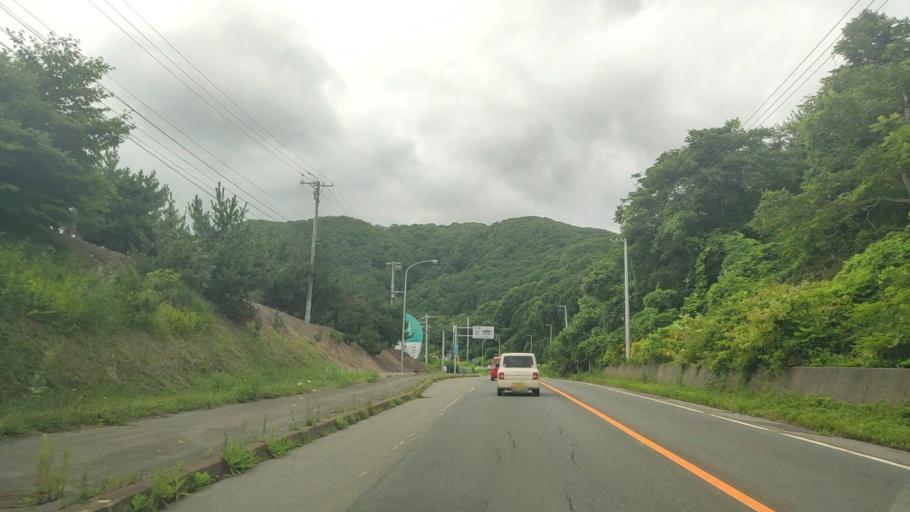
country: JP
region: Hokkaido
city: Date
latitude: 42.5593
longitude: 140.7463
